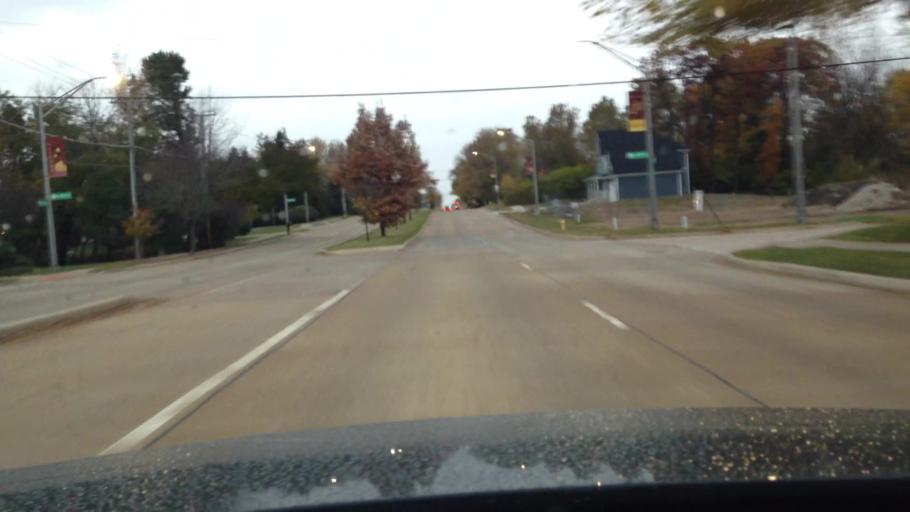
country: US
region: Illinois
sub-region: DuPage County
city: Lombard
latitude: 41.8470
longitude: -88.0165
